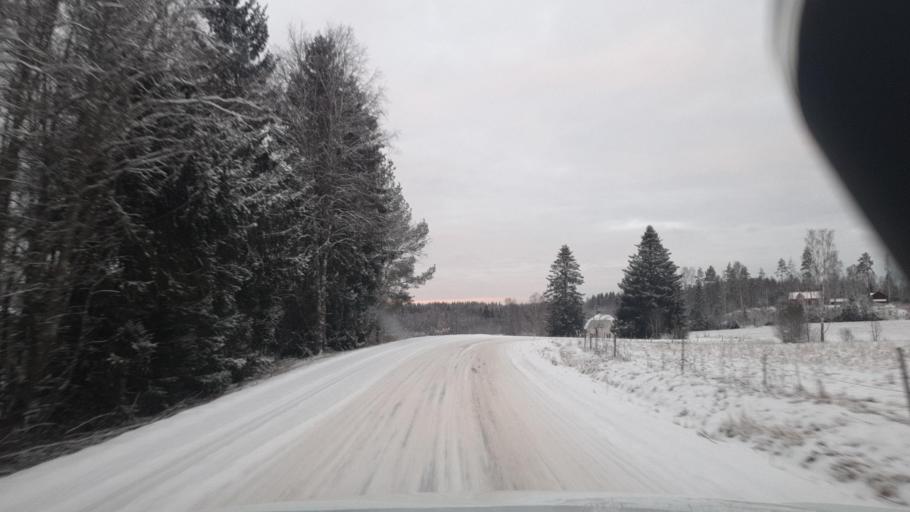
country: SE
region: Vaermland
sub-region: Eda Kommun
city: Charlottenberg
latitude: 59.7646
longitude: 12.2094
